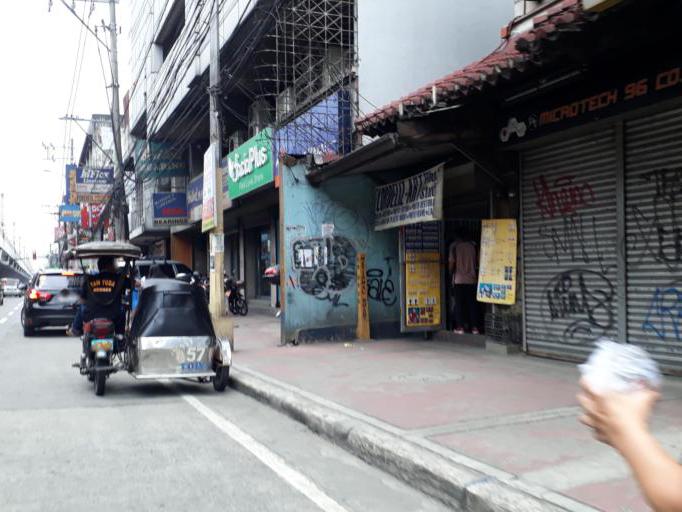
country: PH
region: Metro Manila
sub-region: Caloocan City
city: Niugan
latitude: 14.6528
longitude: 120.9837
